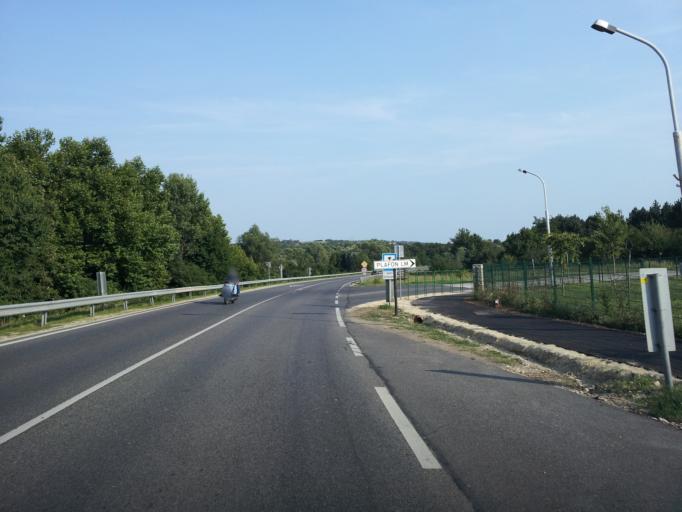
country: HU
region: Veszprem
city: Liter
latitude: 47.0853
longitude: 18.0334
